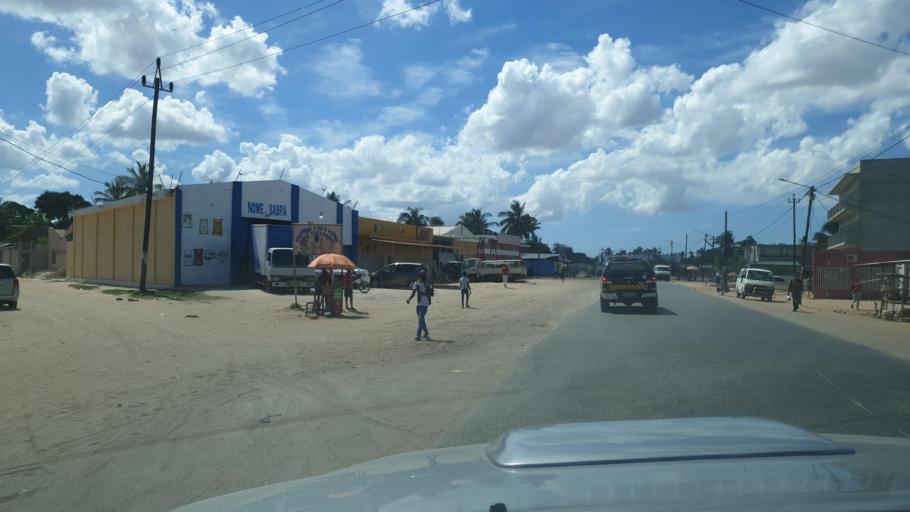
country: MZ
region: Nampula
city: Nacala
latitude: -14.5699
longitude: 40.6859
